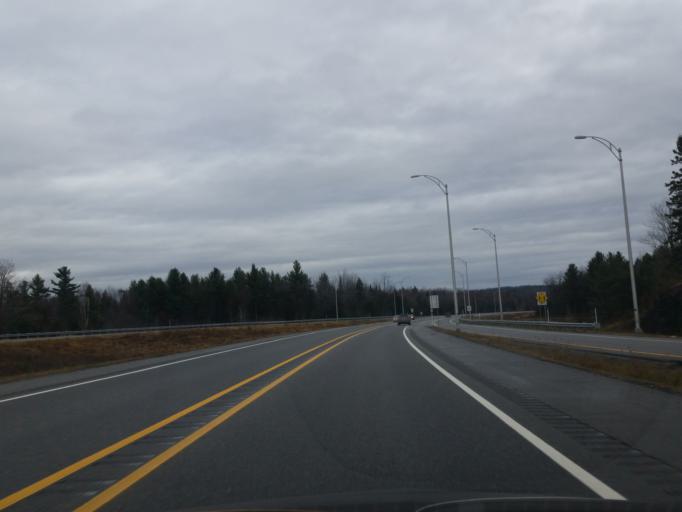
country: CA
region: Ontario
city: Clarence-Rockland
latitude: 45.6101
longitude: -75.3874
